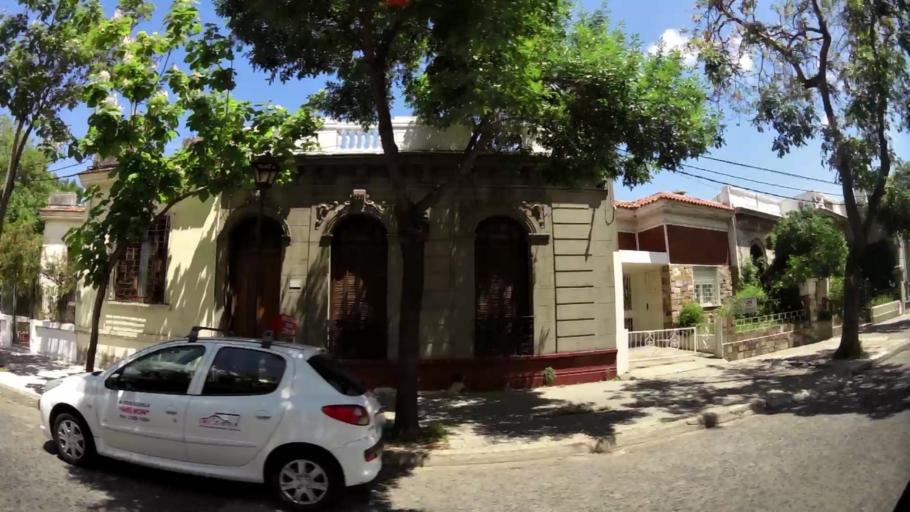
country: UY
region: Montevideo
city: Montevideo
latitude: -34.8707
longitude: -56.2007
